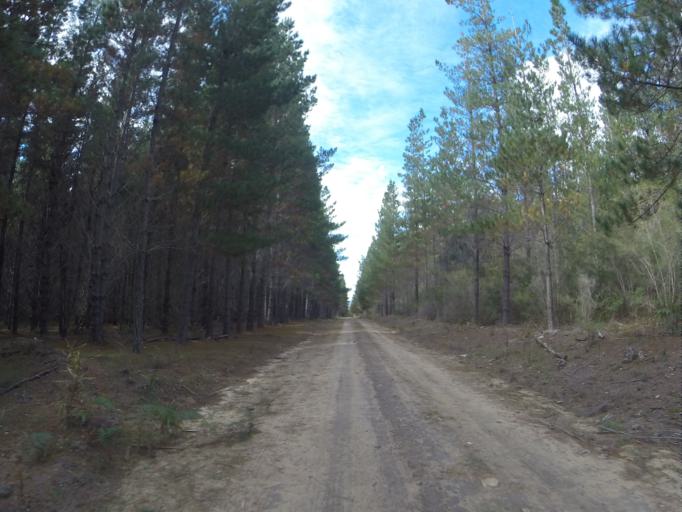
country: AU
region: New South Wales
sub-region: Wingecarribee
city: Moss Vale
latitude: -34.5137
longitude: 150.2331
